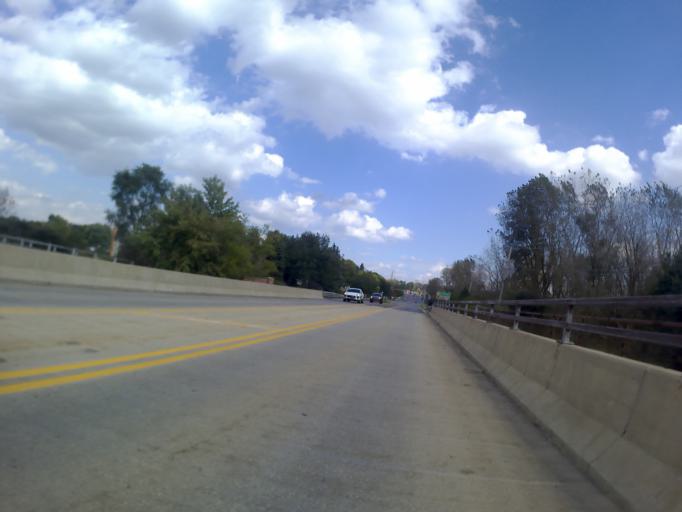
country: US
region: Illinois
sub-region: DuPage County
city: Woodridge
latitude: 41.7591
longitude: -88.0723
